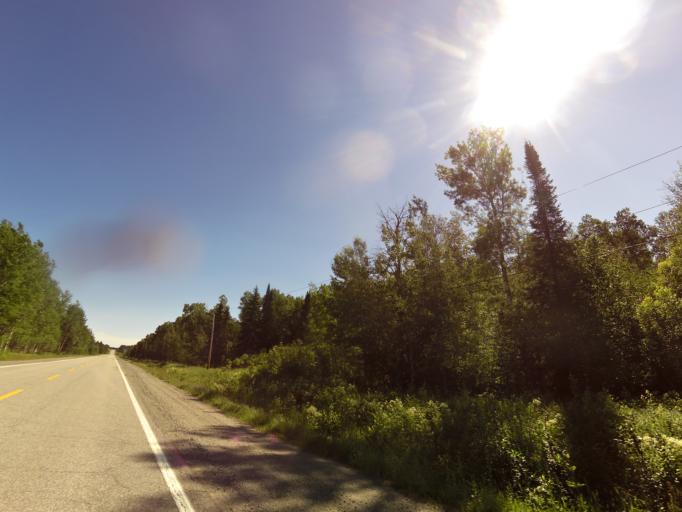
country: CA
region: Quebec
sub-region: Abitibi-Temiscamingue
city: Senneterre
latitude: 48.1636
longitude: -77.3645
